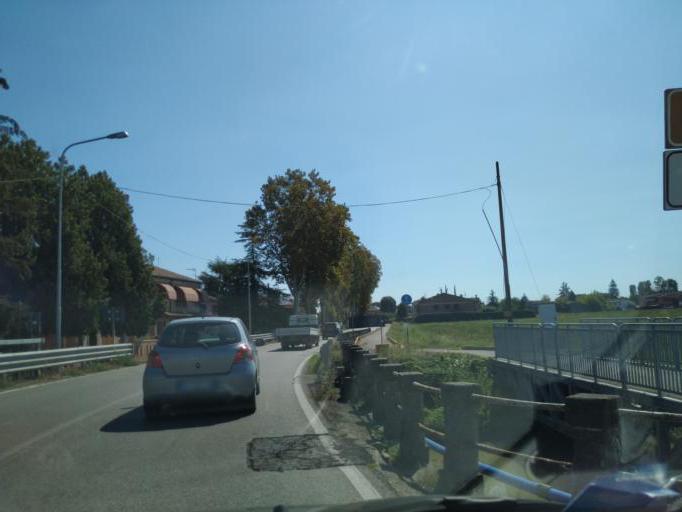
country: IT
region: Emilia-Romagna
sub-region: Provincia di Ferrara
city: La Saletta-Tamara
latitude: 44.8821
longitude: 11.7468
